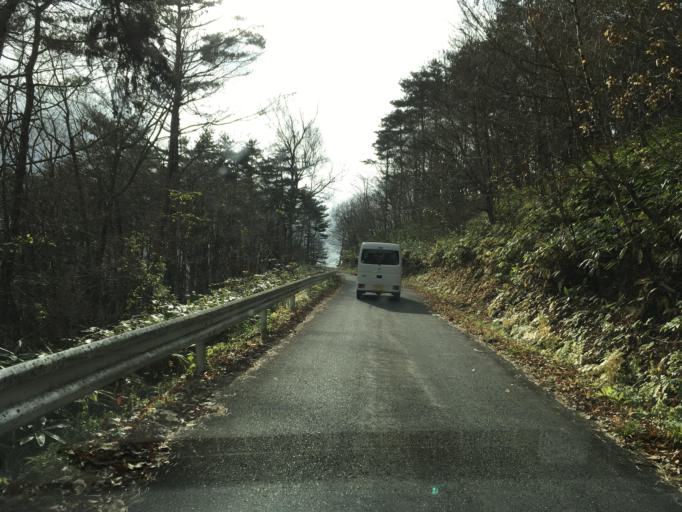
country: JP
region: Iwate
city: Mizusawa
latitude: 39.1248
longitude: 141.3046
